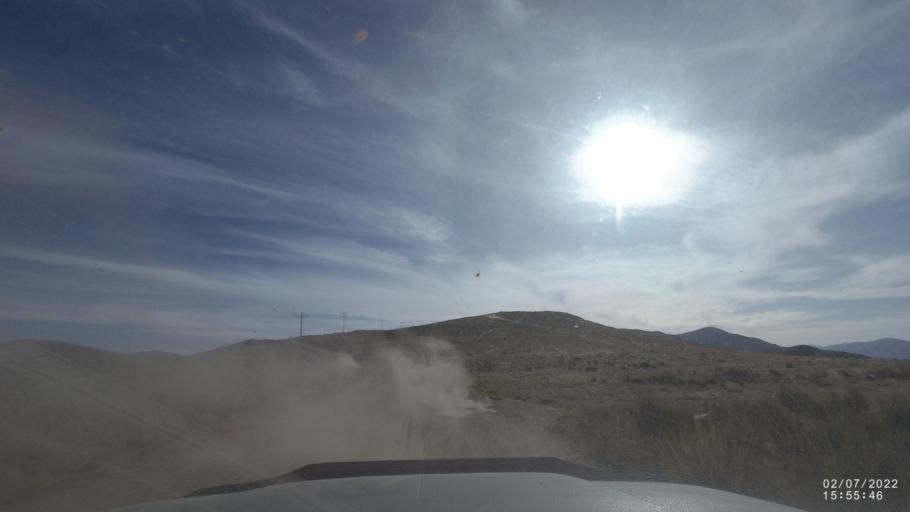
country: BO
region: Cochabamba
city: Irpa Irpa
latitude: -17.9092
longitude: -66.4220
